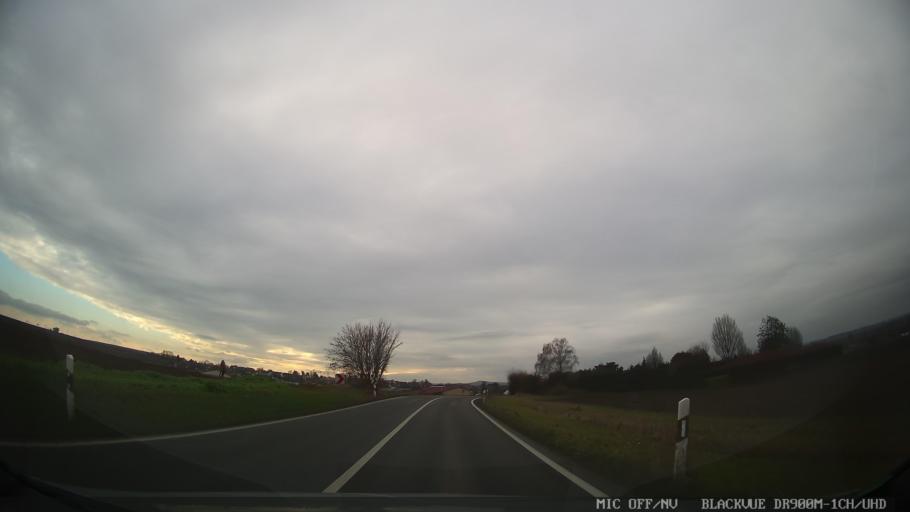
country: DE
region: Rheinland-Pfalz
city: Kongernheim
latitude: 49.8521
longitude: 8.2518
